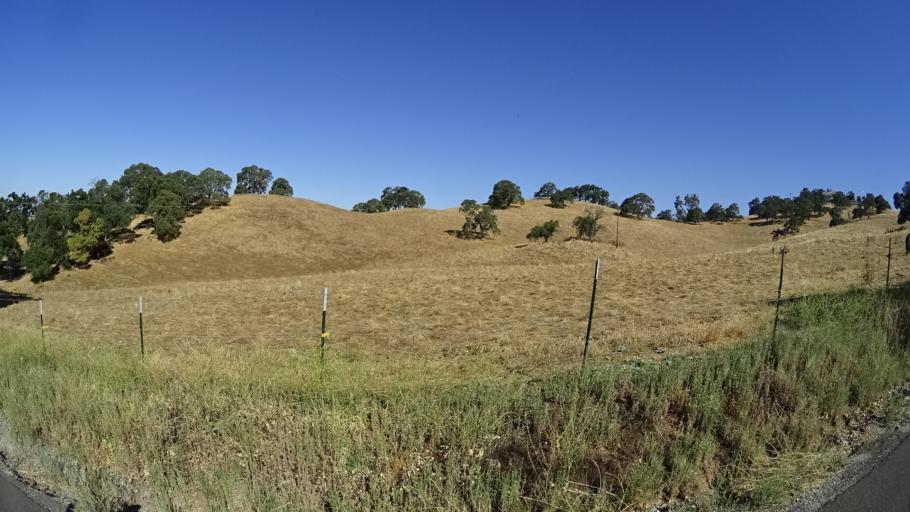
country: US
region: California
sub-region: Calaveras County
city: San Andreas
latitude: 38.2240
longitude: -120.6803
